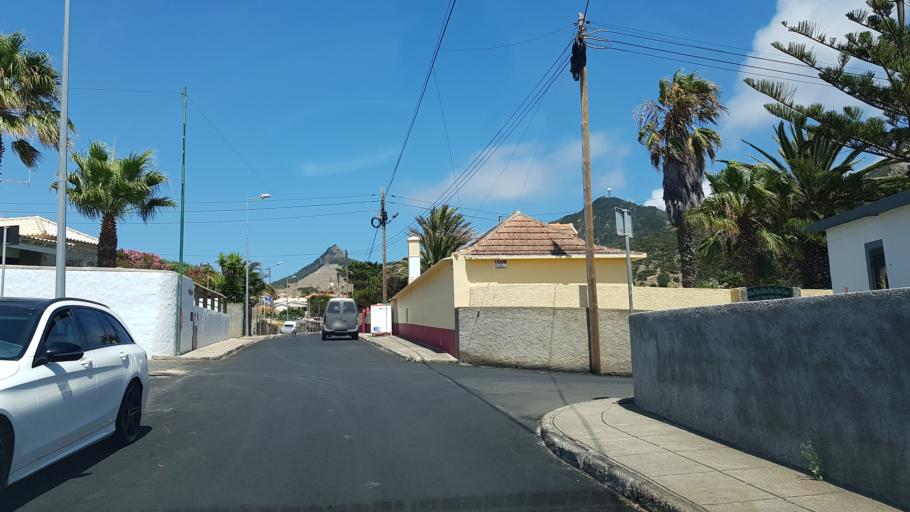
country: PT
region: Madeira
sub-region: Porto Santo
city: Camacha
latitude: 33.0859
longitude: -16.3455
